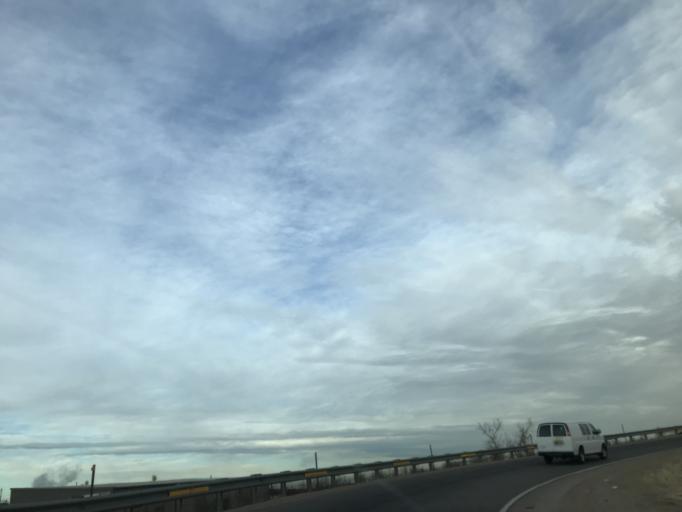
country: US
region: Colorado
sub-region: Adams County
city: Commerce City
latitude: 39.7997
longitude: -104.9348
